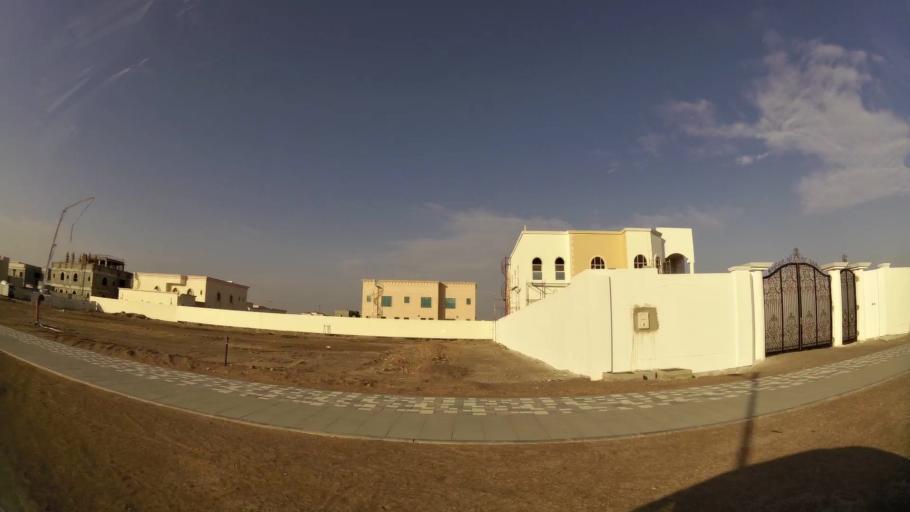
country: AE
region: Abu Dhabi
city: Al Ain
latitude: 24.0959
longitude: 55.8524
